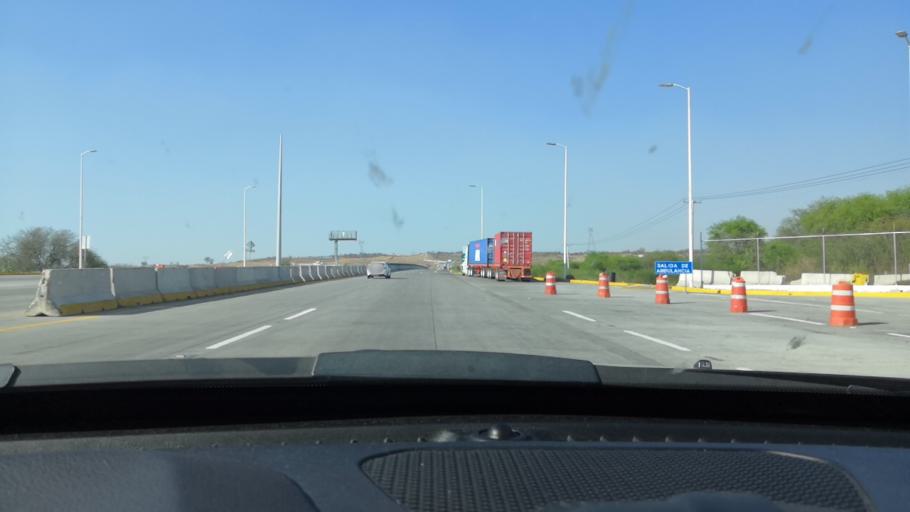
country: MX
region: Jalisco
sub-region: Zapotlanejo
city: La Mezquitera
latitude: 20.5733
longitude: -103.1012
